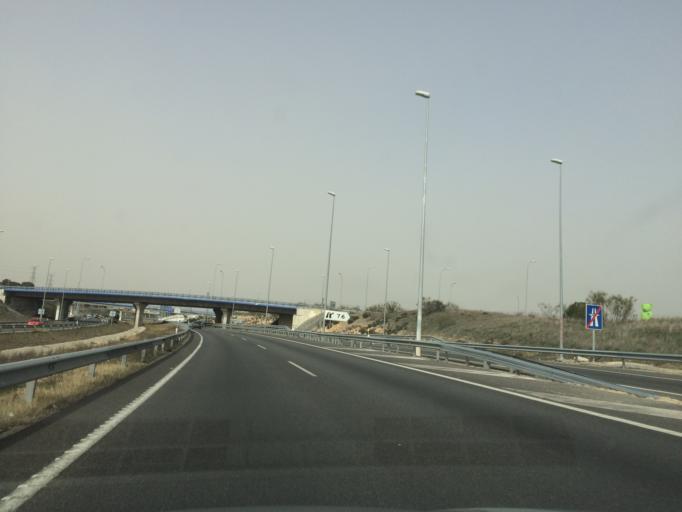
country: ES
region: Madrid
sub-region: Provincia de Madrid
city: Majadahonda
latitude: 40.4411
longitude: -3.8774
